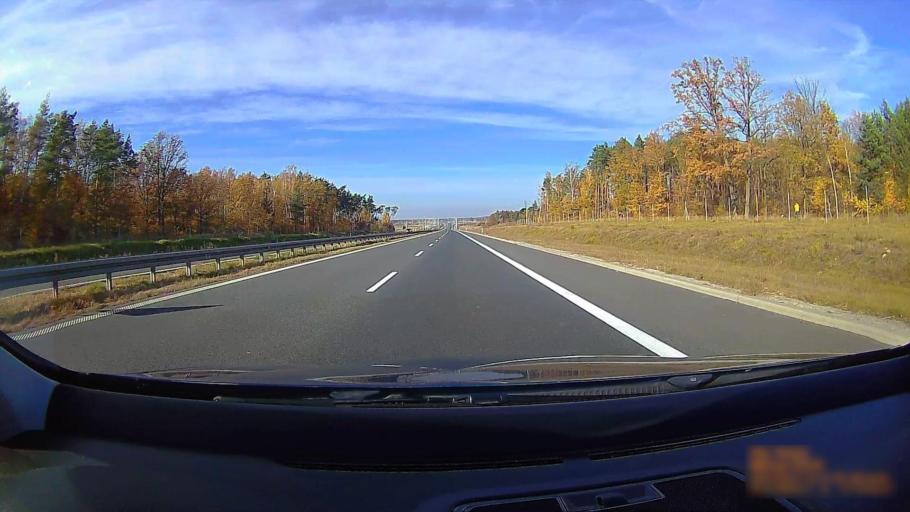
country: PL
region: Greater Poland Voivodeship
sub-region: Powiat ostrowski
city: Ostrow Wielkopolski
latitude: 51.6566
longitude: 17.8646
